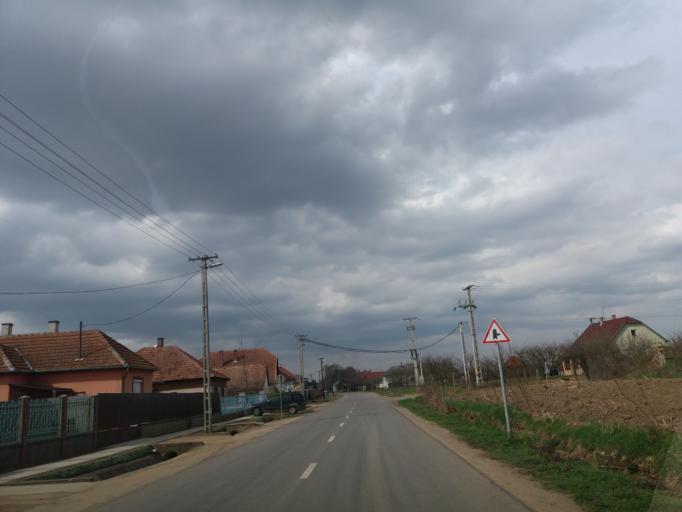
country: HU
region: Szabolcs-Szatmar-Bereg
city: Nyirtass
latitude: 48.1041
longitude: 22.0277
